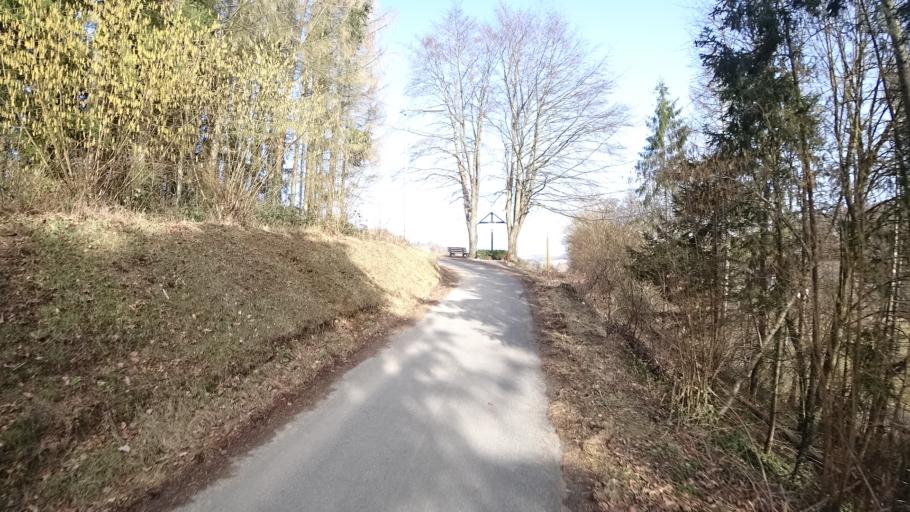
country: DE
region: Rheinland-Pfalz
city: Elben
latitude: 50.7368
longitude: 7.8264
